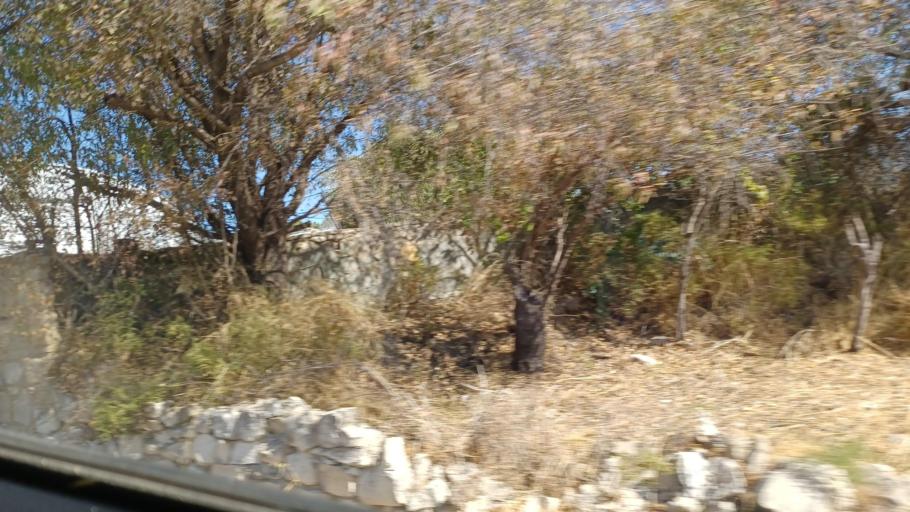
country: CY
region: Pafos
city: Mesogi
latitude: 34.9226
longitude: 32.5715
